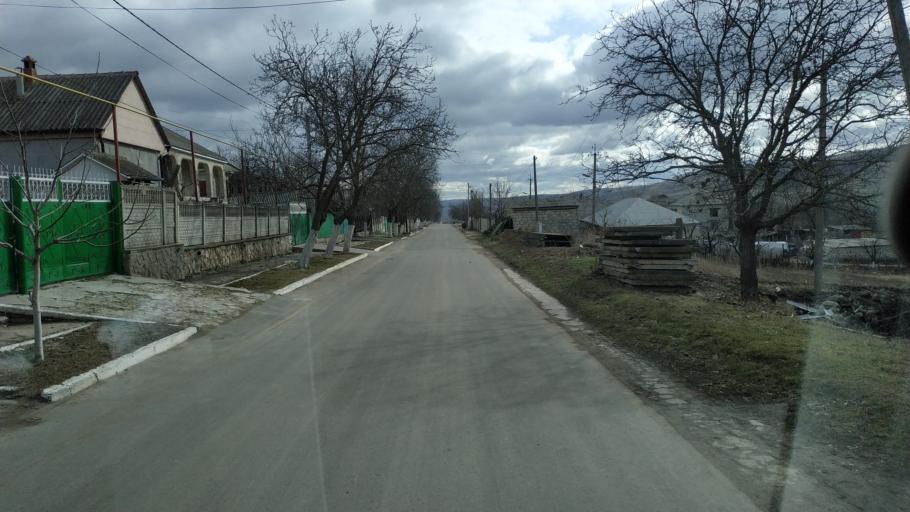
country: MD
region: Stinga Nistrului
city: Bucovat
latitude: 47.2251
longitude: 28.4371
